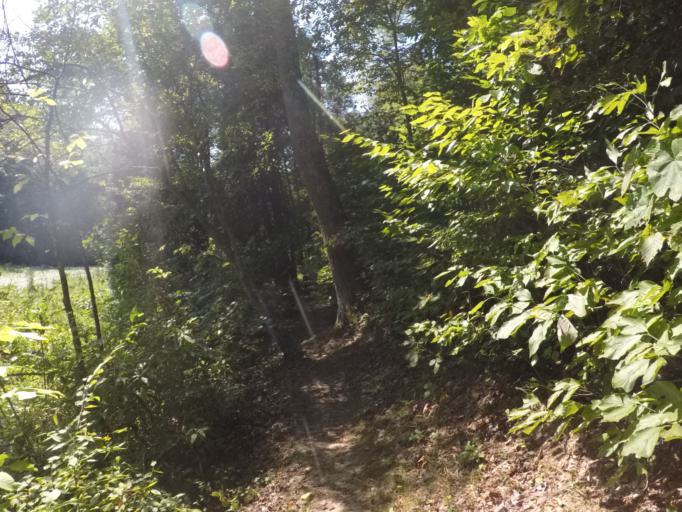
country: US
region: Ohio
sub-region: Lawrence County
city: Ironton
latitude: 38.6245
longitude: -82.6182
